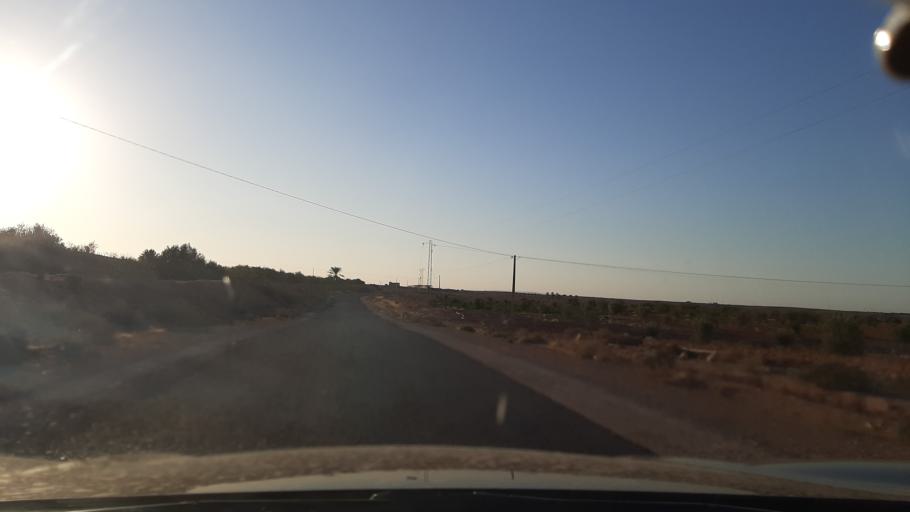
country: TN
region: Qabis
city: Matmata
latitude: 33.6191
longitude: 10.1456
